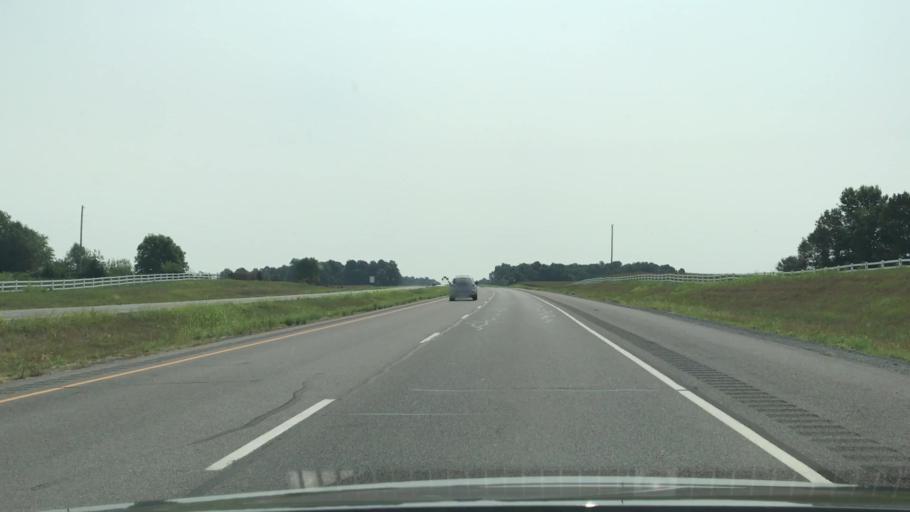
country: US
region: Kentucky
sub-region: Graves County
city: Mayfield
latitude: 36.6788
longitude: -88.5272
